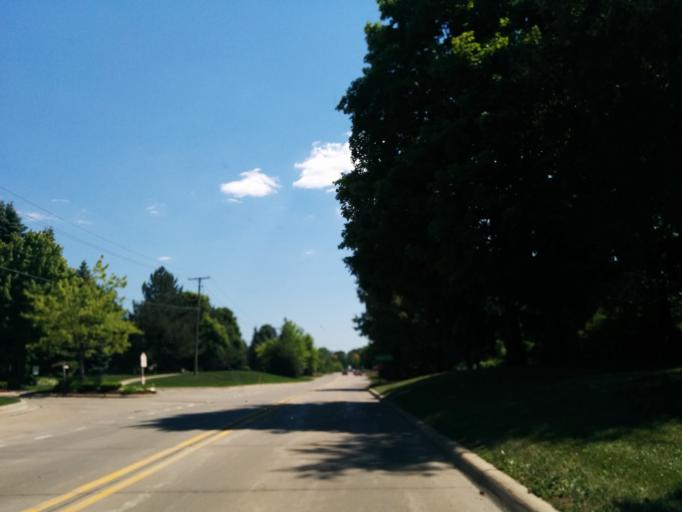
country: US
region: Michigan
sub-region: Oakland County
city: Farmington Hills
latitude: 42.5144
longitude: -83.4181
